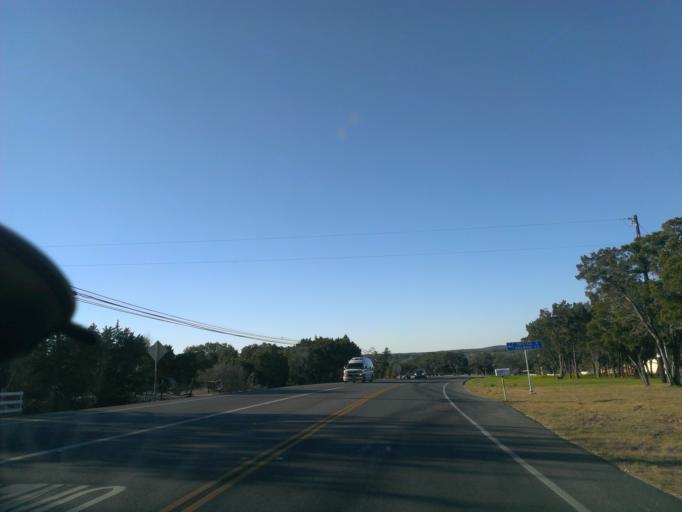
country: US
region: Texas
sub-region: Hays County
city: Dripping Springs
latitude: 30.1715
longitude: -98.0859
